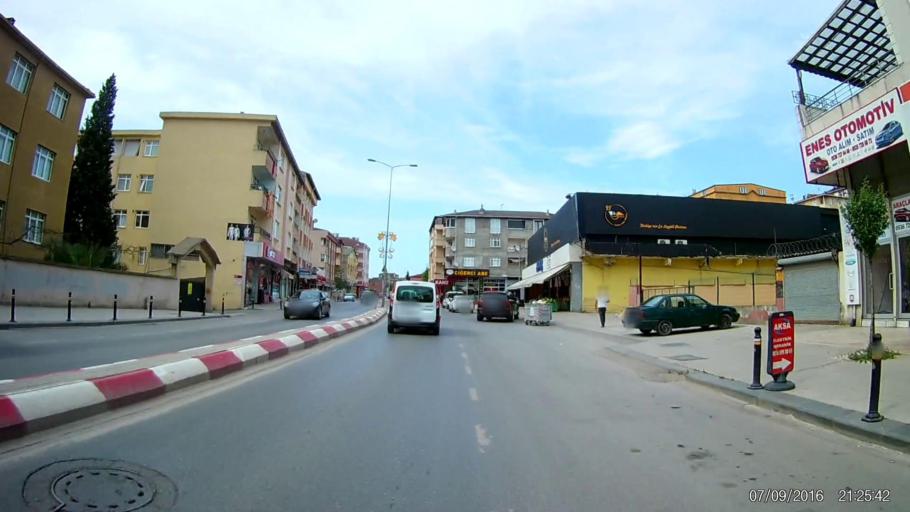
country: TR
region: Istanbul
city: Sultanbeyli
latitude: 40.9790
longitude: 29.2658
